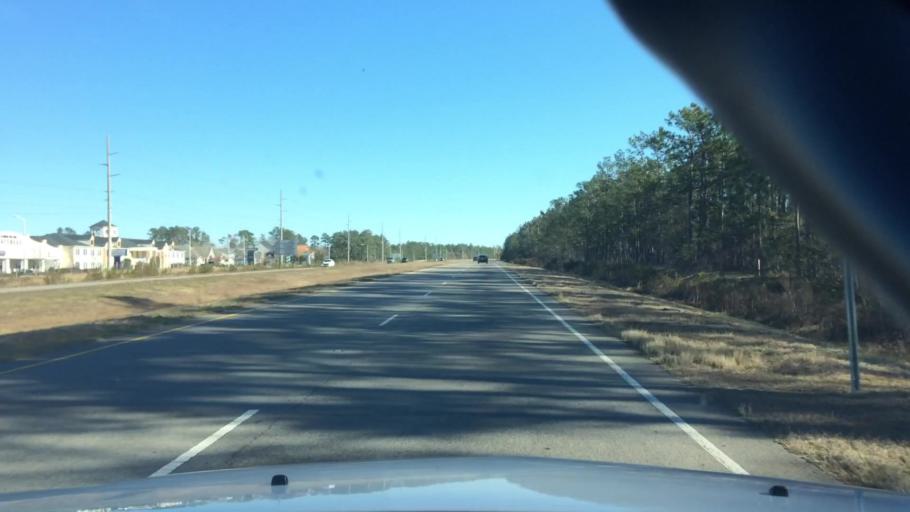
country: US
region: North Carolina
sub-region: Brunswick County
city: Shallotte
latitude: 33.9827
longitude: -78.3964
